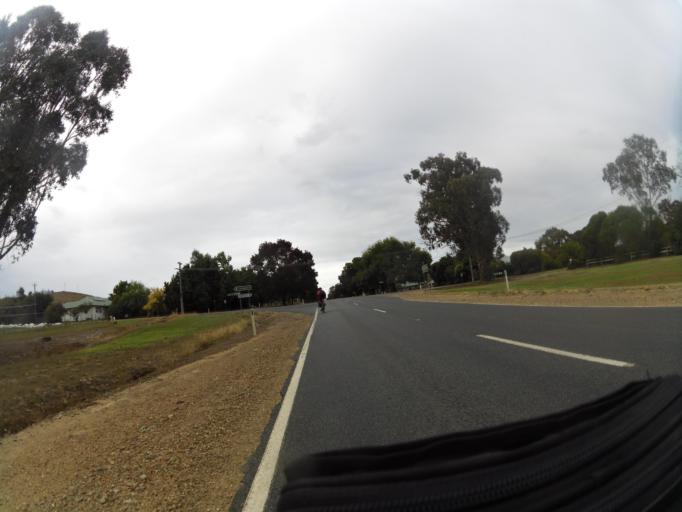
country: AU
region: New South Wales
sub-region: Snowy River
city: Jindabyne
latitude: -36.1868
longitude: 147.9175
